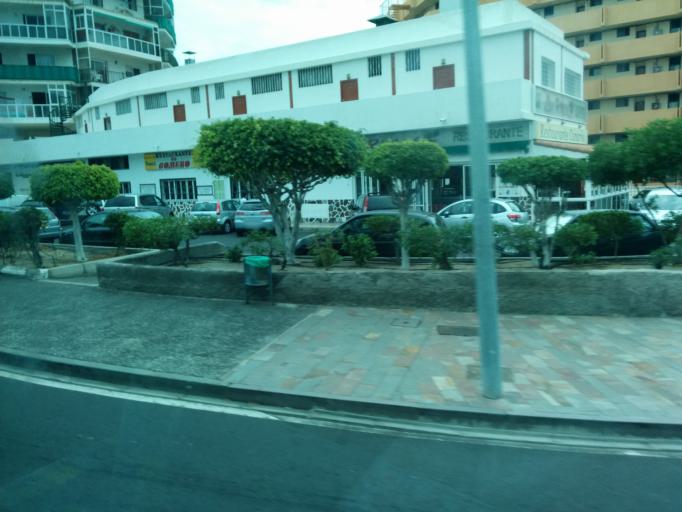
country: ES
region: Canary Islands
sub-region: Provincia de Santa Cruz de Tenerife
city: Playa de las Americas
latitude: 28.0682
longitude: -16.7269
